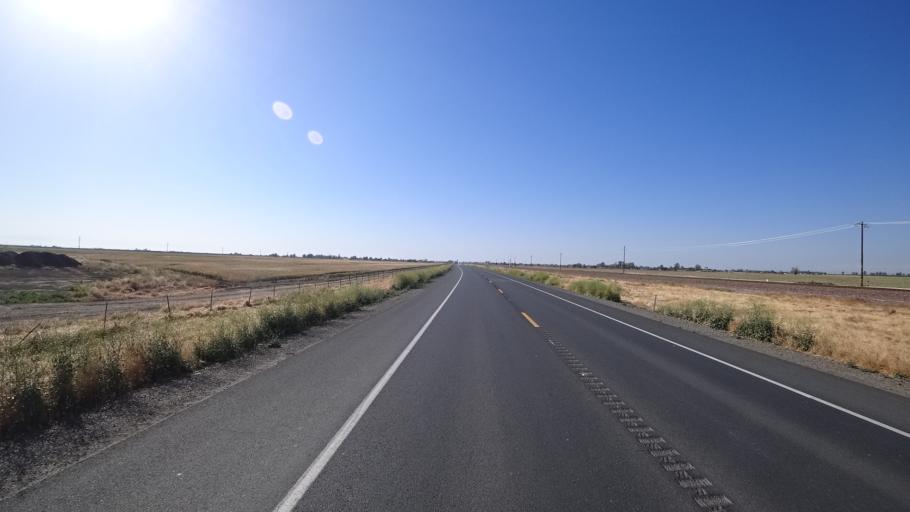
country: US
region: California
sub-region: Kings County
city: Corcoran
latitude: 36.1298
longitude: -119.5792
